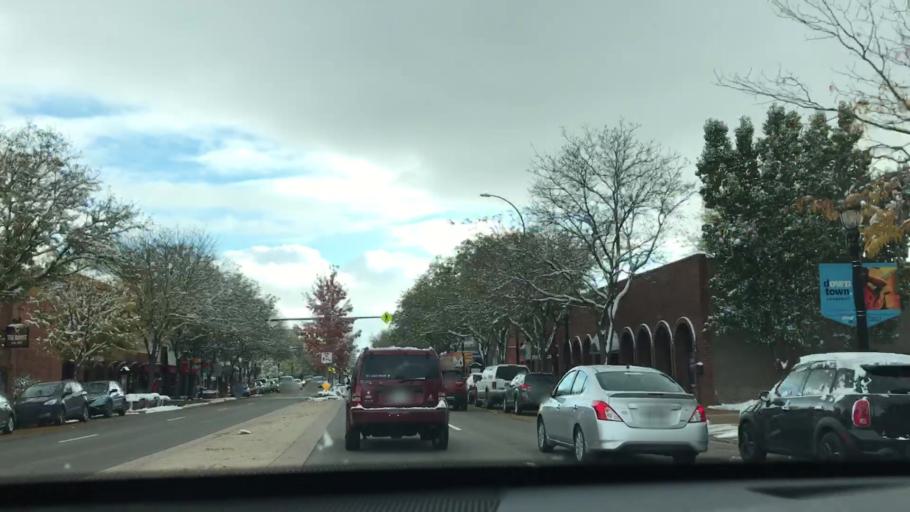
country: US
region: Colorado
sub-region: Boulder County
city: Longmont
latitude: 40.1687
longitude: -105.1025
